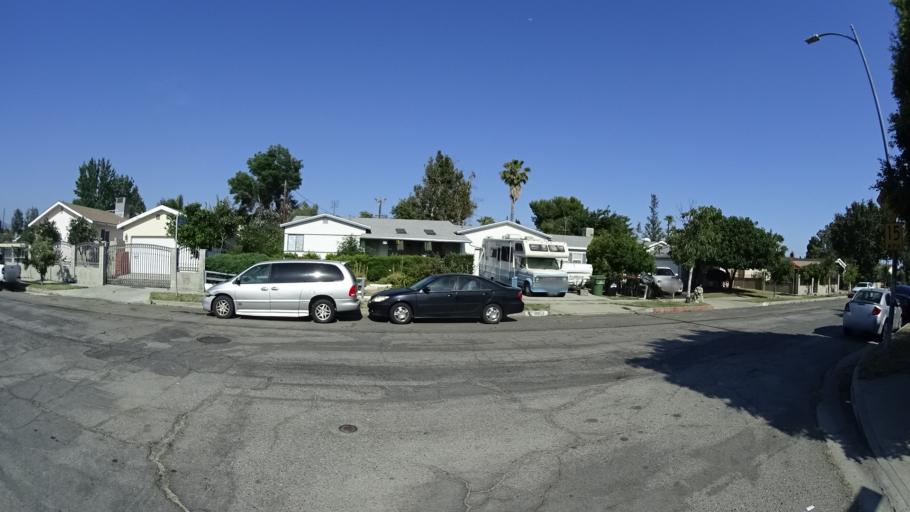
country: US
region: California
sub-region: Los Angeles County
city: Van Nuys
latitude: 34.2175
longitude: -118.4228
